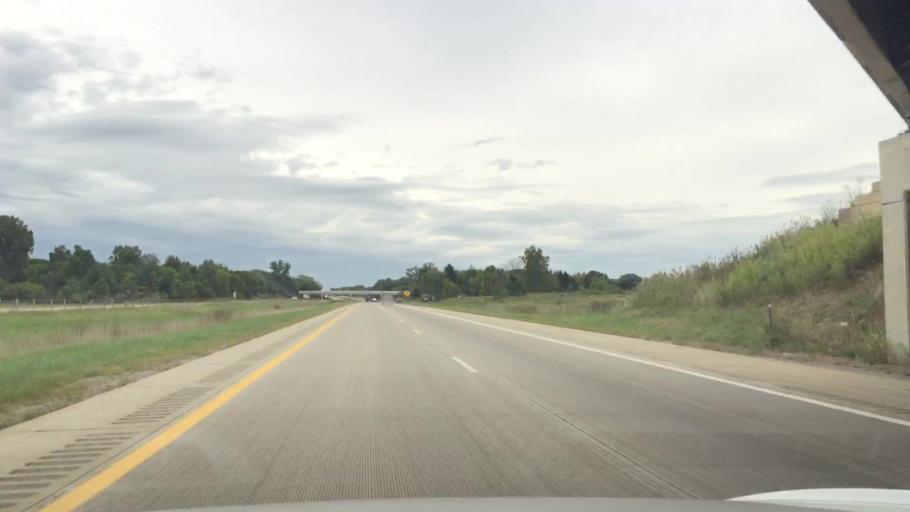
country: US
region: Michigan
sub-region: Macomb County
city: Richmond
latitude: 42.8130
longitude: -82.6286
